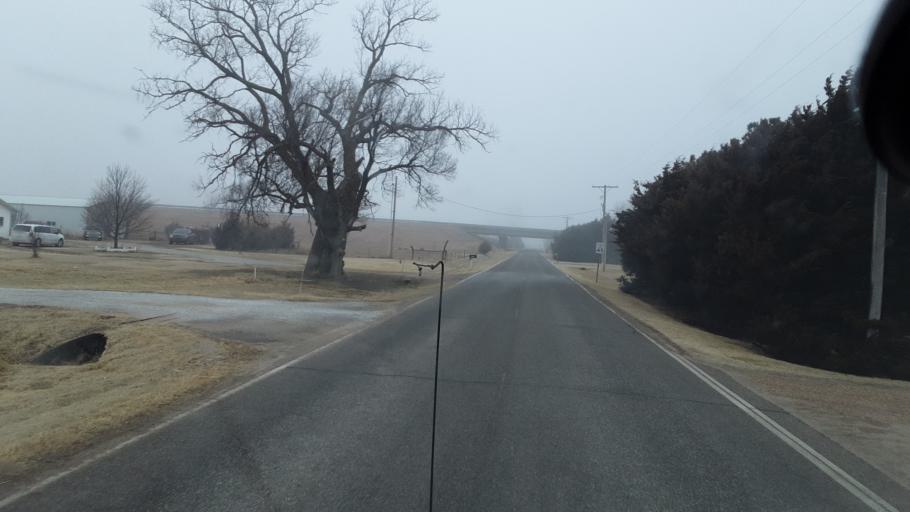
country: US
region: Kansas
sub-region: Reno County
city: Haven
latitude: 37.9410
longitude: -97.8783
